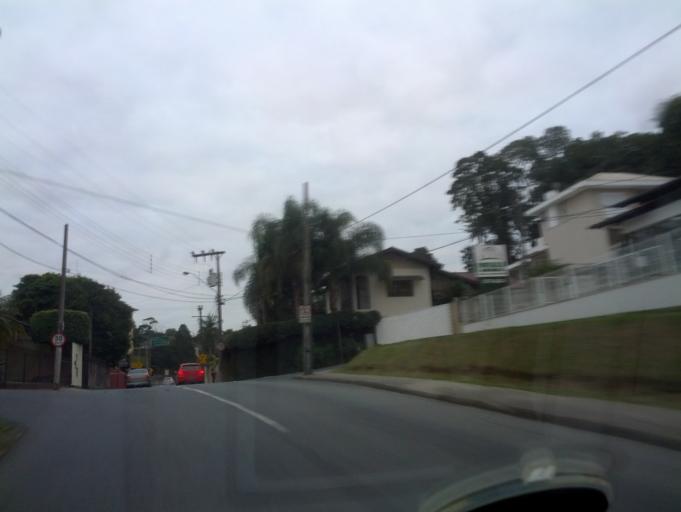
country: BR
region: Santa Catarina
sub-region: Blumenau
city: Blumenau
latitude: -26.8784
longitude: -49.0809
